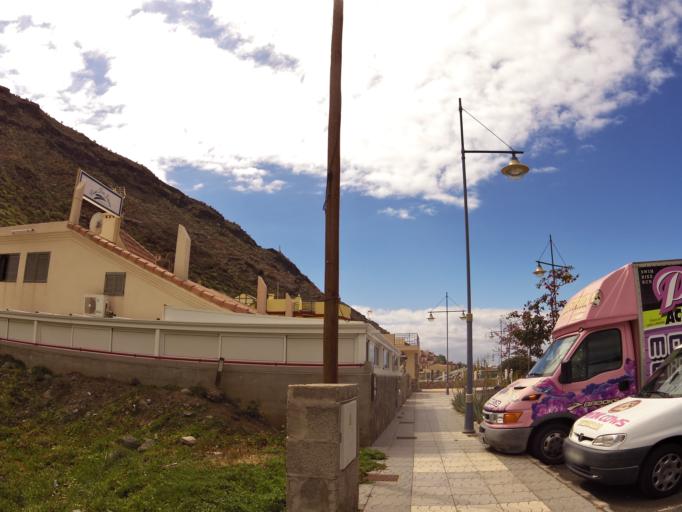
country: ES
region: Canary Islands
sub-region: Provincia de Las Palmas
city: Puerto Rico
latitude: 27.8274
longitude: -15.7556
